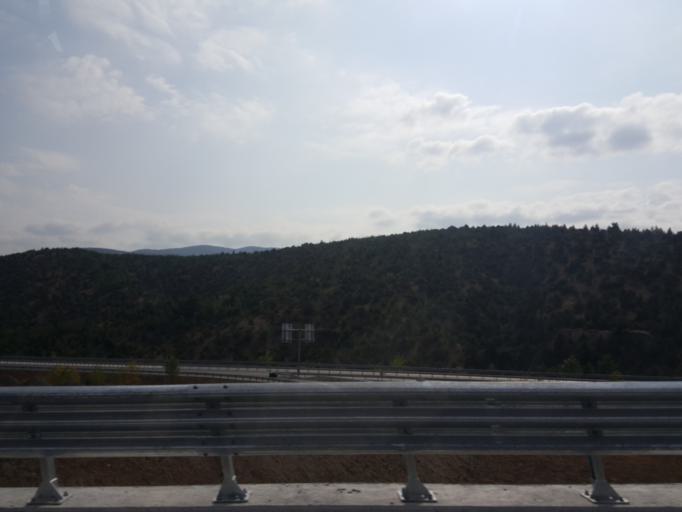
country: TR
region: Corum
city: Hacihamza
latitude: 41.0997
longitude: 34.3621
